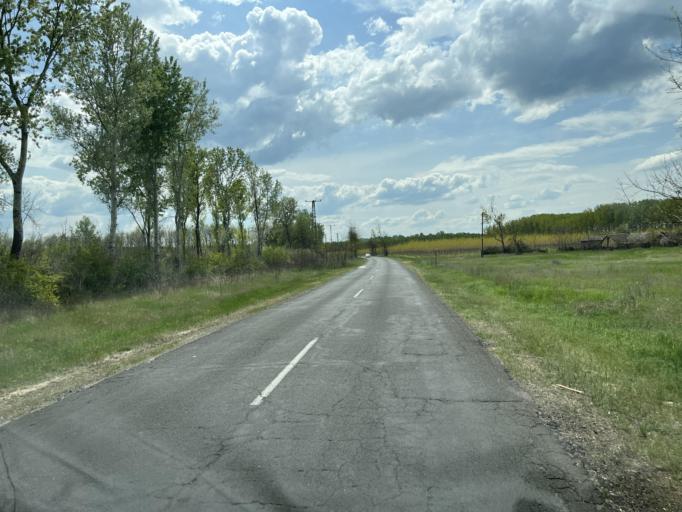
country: HU
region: Pest
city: Csemo
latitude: 47.1261
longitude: 19.6556
